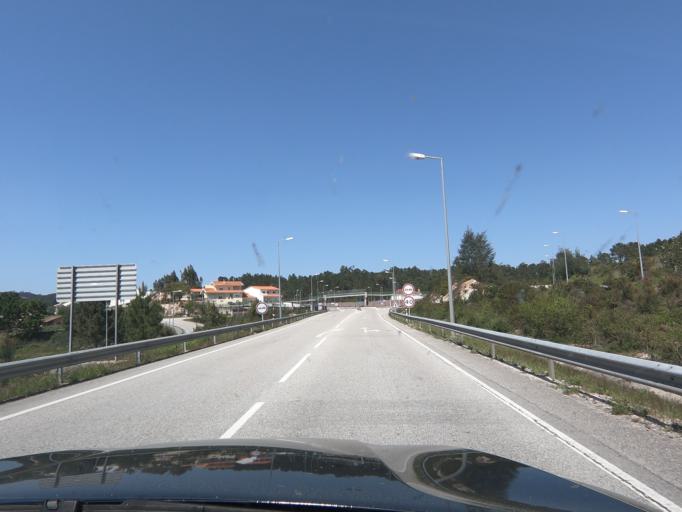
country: PT
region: Coimbra
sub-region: Miranda do Corvo
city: Miranda do Corvo
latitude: 40.0901
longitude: -8.3168
